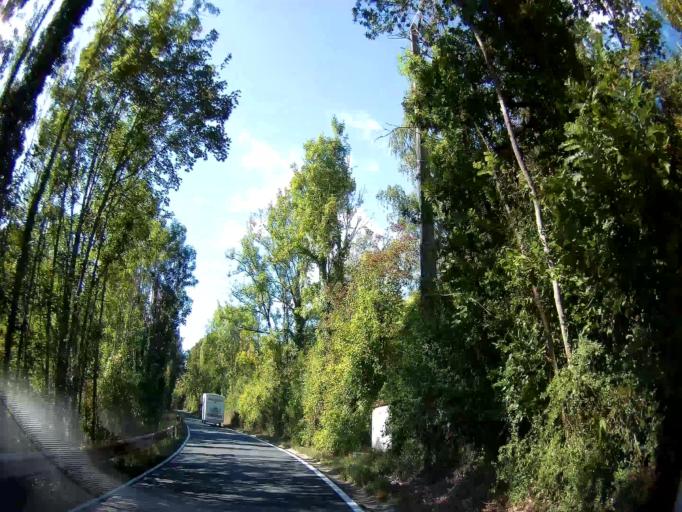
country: BE
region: Wallonia
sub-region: Province de Namur
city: Mettet
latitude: 50.3153
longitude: 4.7607
